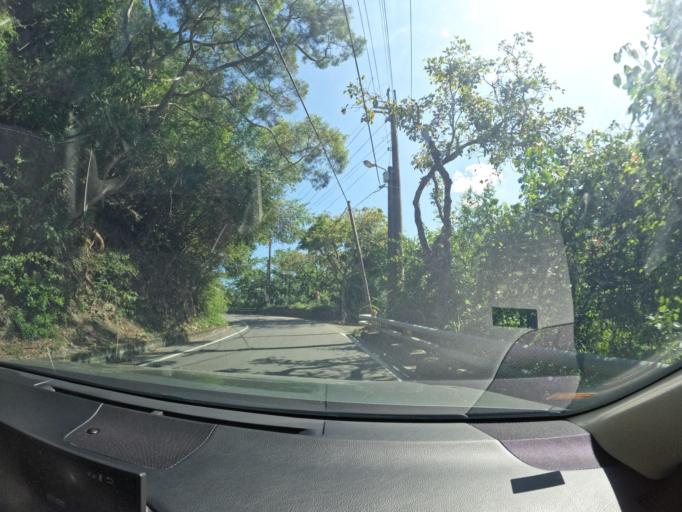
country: TW
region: Taiwan
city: Yujing
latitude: 23.1538
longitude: 120.7603
